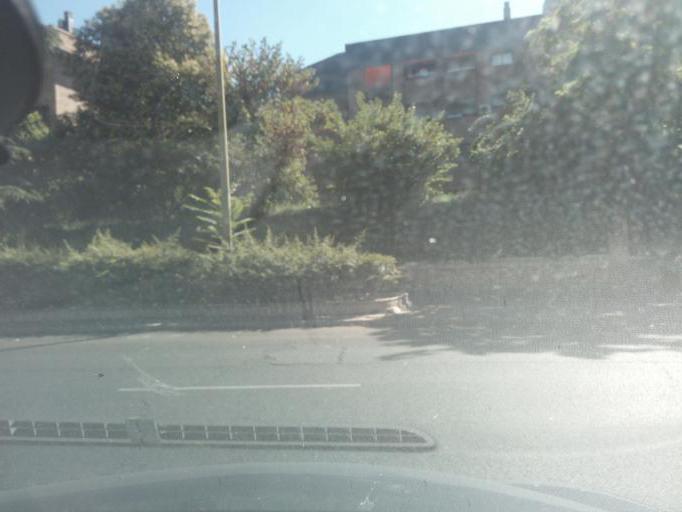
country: ES
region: Madrid
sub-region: Provincia de Madrid
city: Pinar de Chamartin
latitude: 40.4717
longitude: -3.6674
